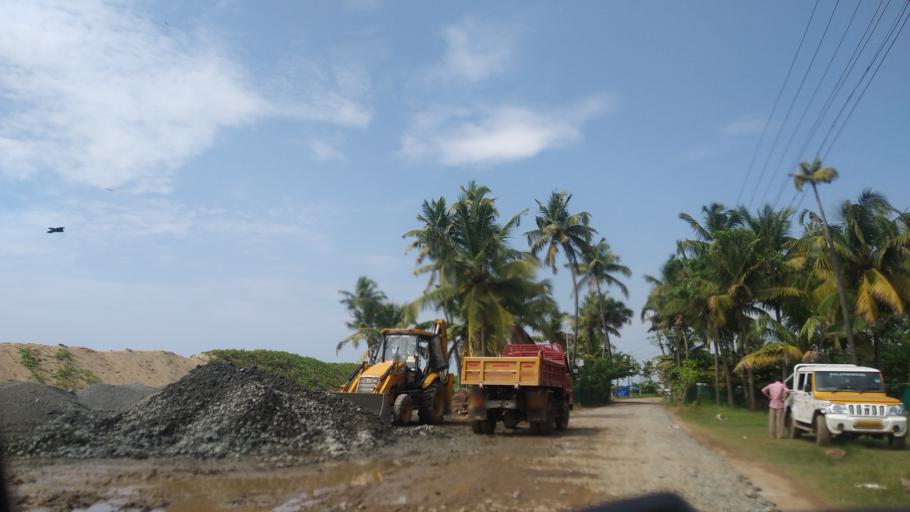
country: IN
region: Kerala
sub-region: Ernakulam
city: Elur
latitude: 10.0594
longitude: 76.2005
